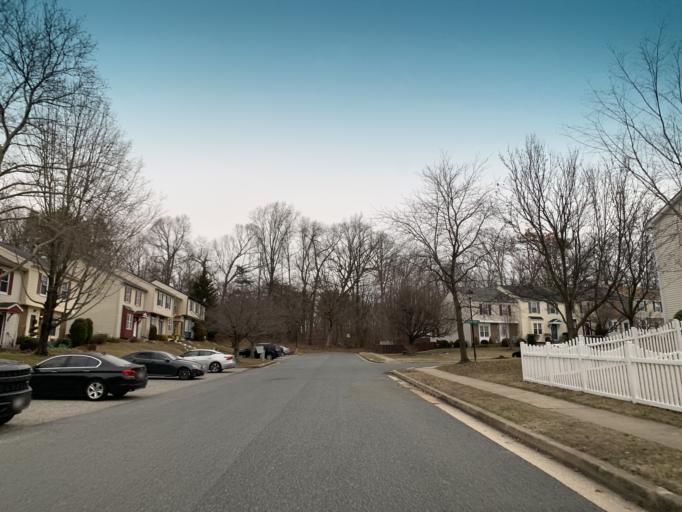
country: US
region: Maryland
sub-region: Baltimore County
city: White Marsh
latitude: 39.3864
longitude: -76.4536
